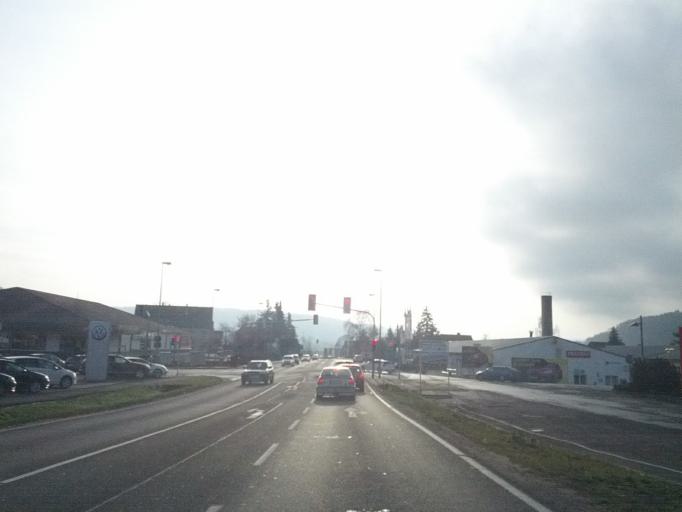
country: DE
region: Thuringia
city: Meiningen
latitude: 50.5892
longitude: 10.4118
